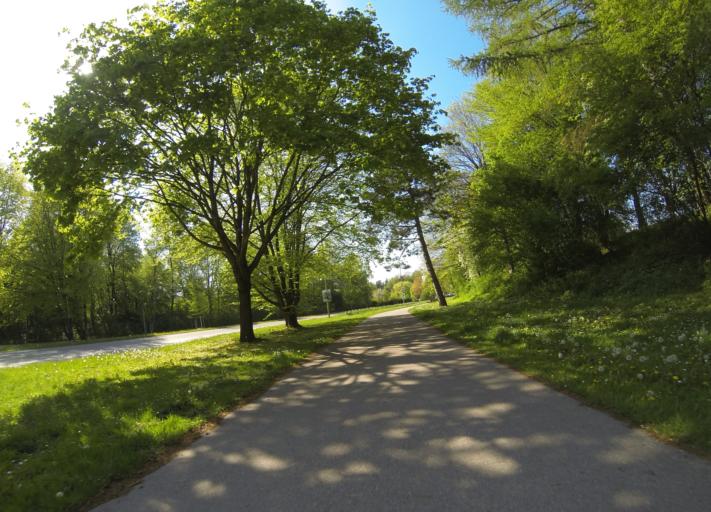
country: DE
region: Baden-Wuerttemberg
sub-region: Tuebingen Region
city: Staig
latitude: 48.3469
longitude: 9.9693
